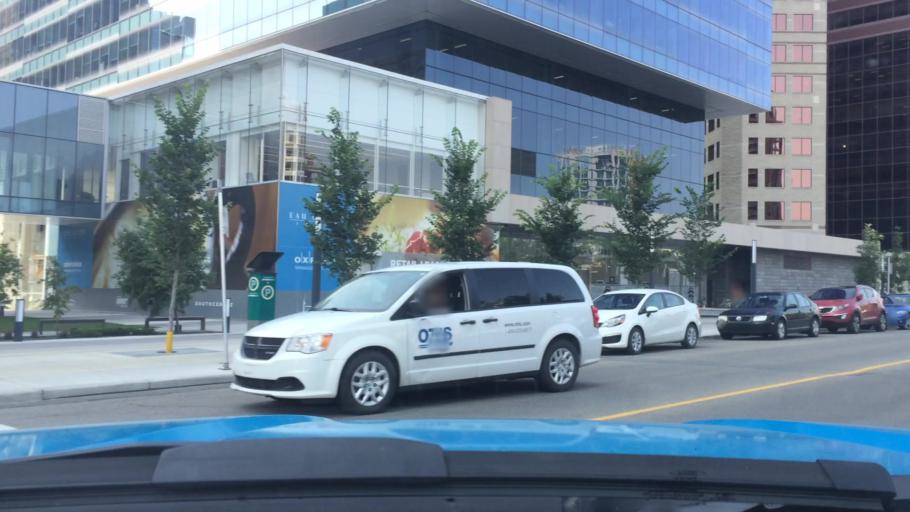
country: CA
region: Alberta
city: Calgary
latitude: 51.0516
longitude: -114.0737
